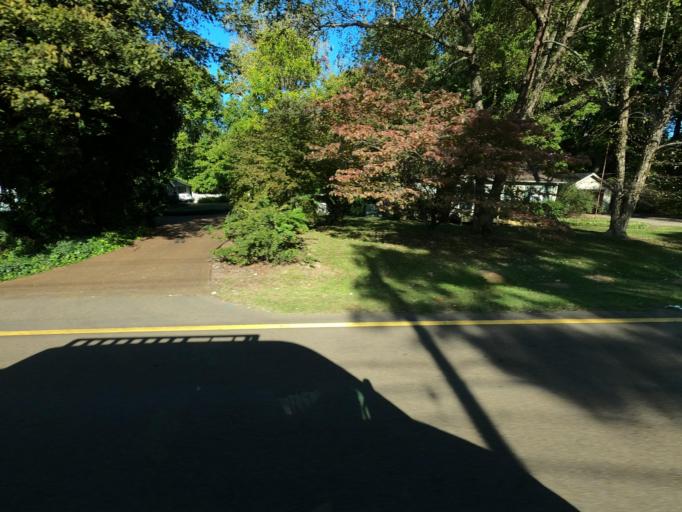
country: US
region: Tennessee
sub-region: Tipton County
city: Atoka
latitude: 35.4398
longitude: -89.7945
